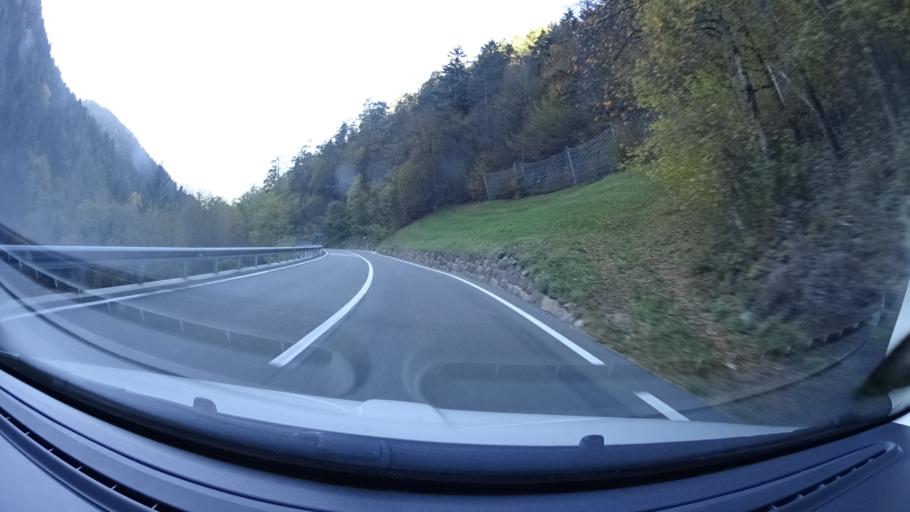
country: IT
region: Trentino-Alto Adige
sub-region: Bolzano
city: Laion
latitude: 46.5960
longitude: 11.5702
